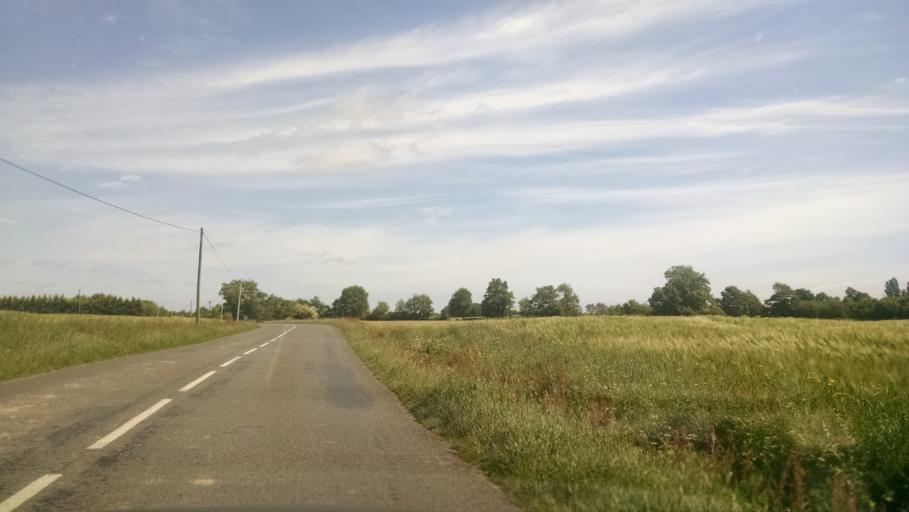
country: FR
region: Pays de la Loire
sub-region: Departement de la Loire-Atlantique
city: Saint-Hilaire-de-Clisson
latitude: 47.0477
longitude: -1.3222
